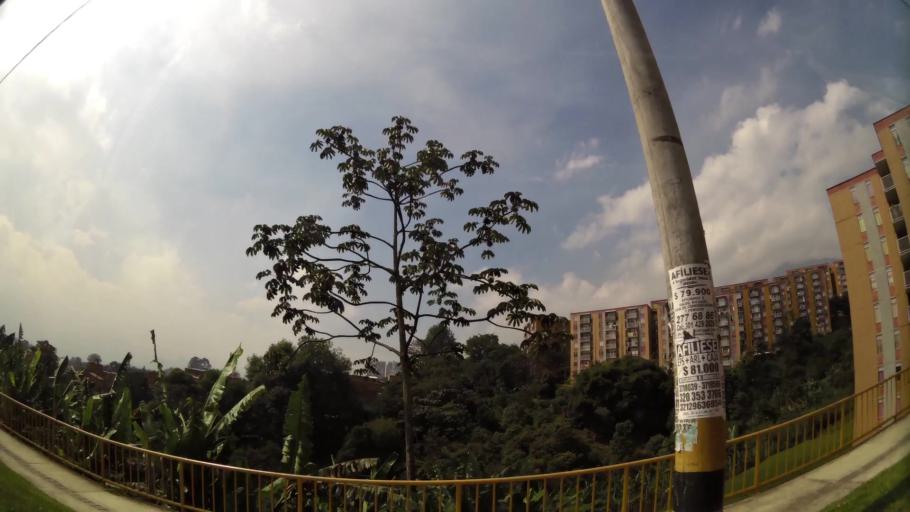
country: CO
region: Antioquia
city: La Estrella
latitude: 6.1744
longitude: -75.6460
